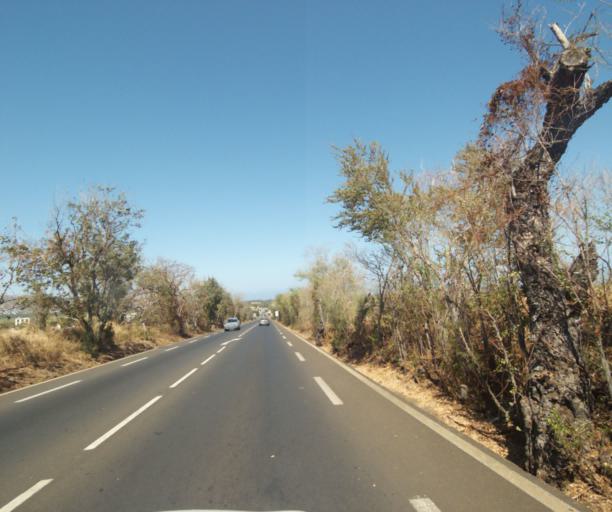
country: RE
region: Reunion
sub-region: Reunion
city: Saint-Paul
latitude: -20.9840
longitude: 55.3016
